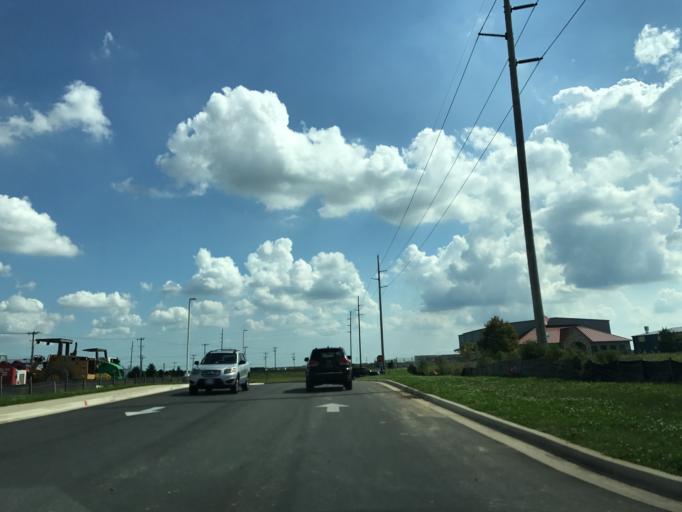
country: US
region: Delaware
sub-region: New Castle County
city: Middletown
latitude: 39.4390
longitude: -75.7473
